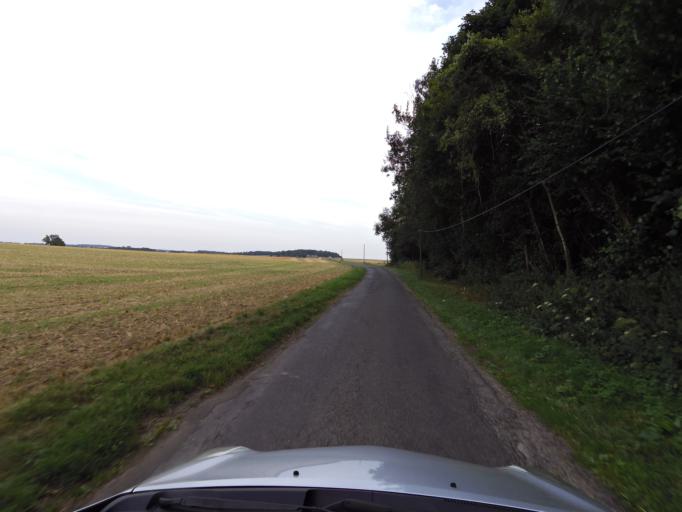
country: FR
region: Picardie
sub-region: Departement de l'Aisne
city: Bruyeres-et-Montberault
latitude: 49.5006
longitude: 3.6503
